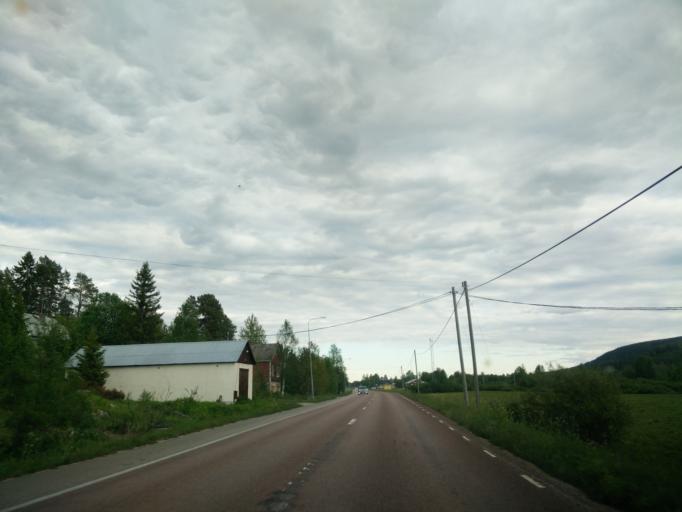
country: SE
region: Jaemtland
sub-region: Harjedalens Kommun
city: Sveg
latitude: 62.2878
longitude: 14.7955
